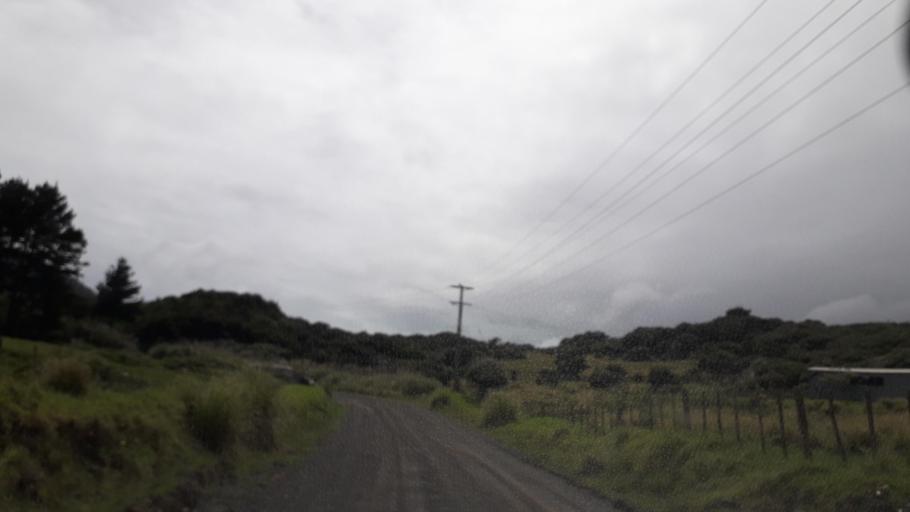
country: NZ
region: Northland
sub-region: Far North District
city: Ahipara
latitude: -35.4370
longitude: 173.3310
